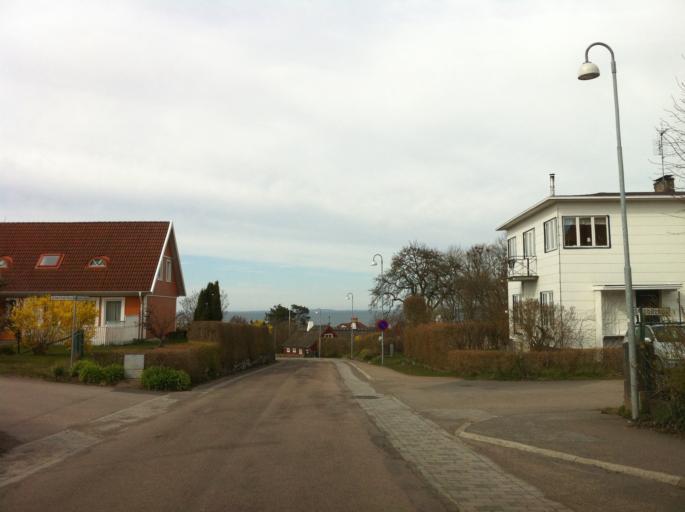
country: SE
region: Skane
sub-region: Hoganas Kommun
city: Hoganas
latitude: 56.2706
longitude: 12.5784
